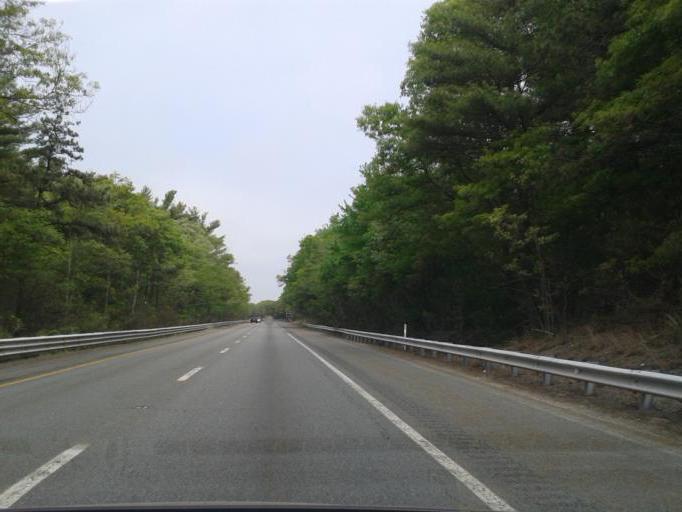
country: US
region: Massachusetts
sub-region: Plymouth County
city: Plymouth
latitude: 41.9256
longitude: -70.6301
